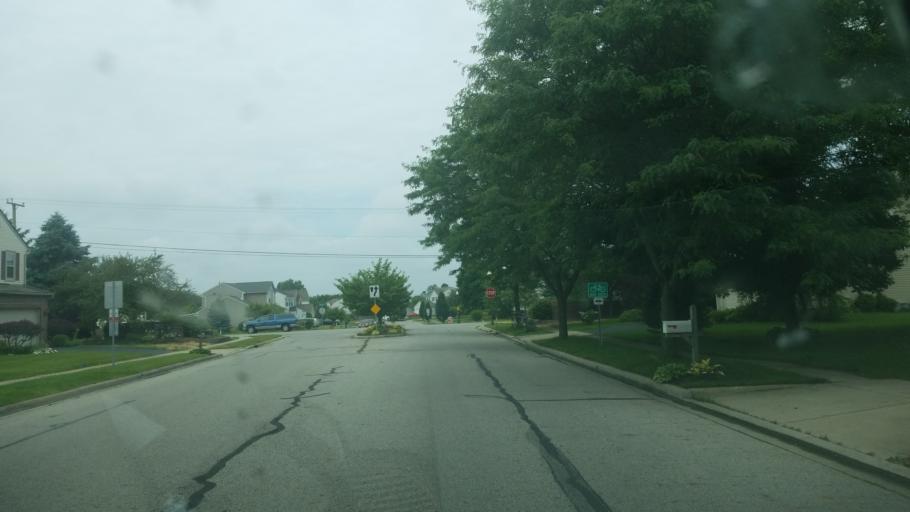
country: US
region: Ohio
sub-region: Franklin County
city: Reynoldsburg
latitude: 40.0070
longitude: -82.7656
